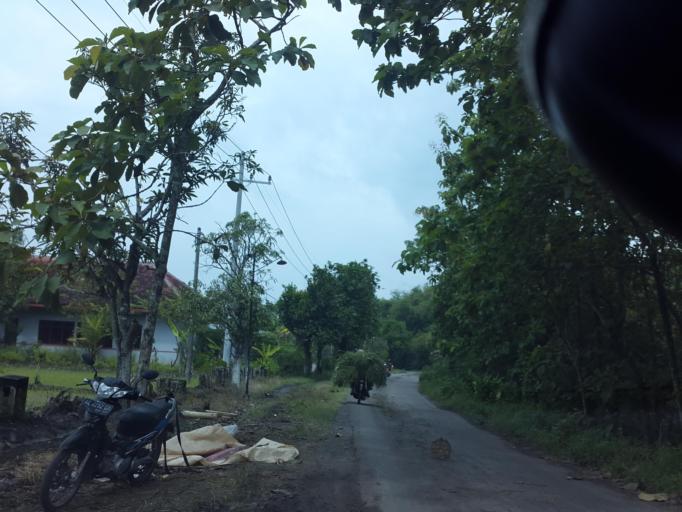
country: ID
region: East Java
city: Madiun
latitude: -7.4844
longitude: 111.6878
